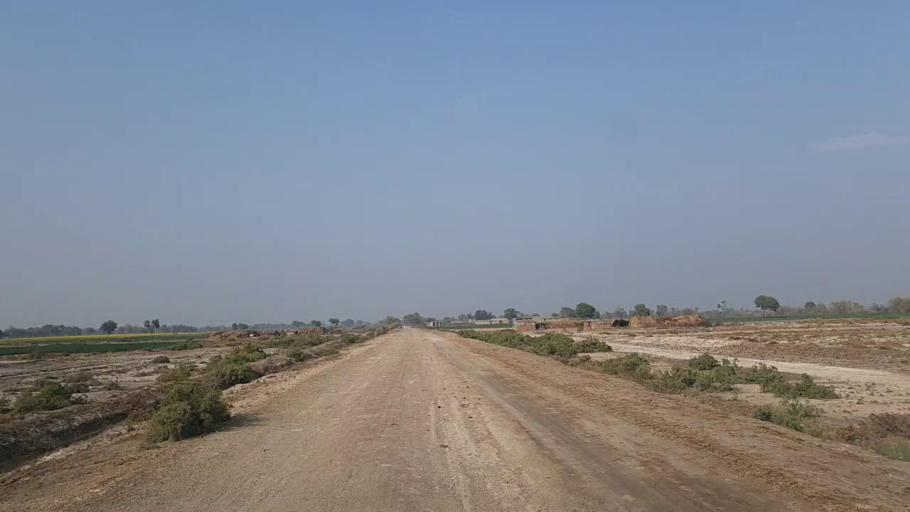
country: PK
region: Sindh
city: Nawabshah
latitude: 26.3458
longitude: 68.4740
